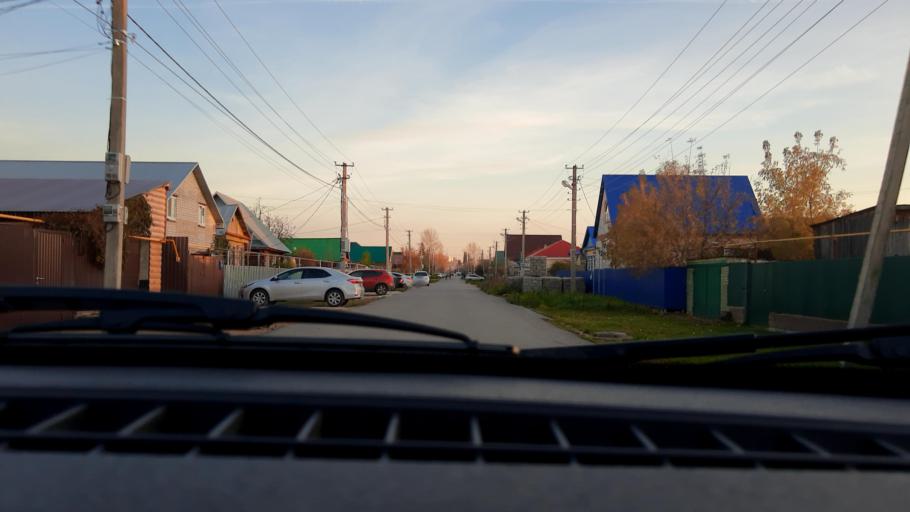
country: RU
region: Bashkortostan
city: Mikhaylovka
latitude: 54.7682
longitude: 55.8997
